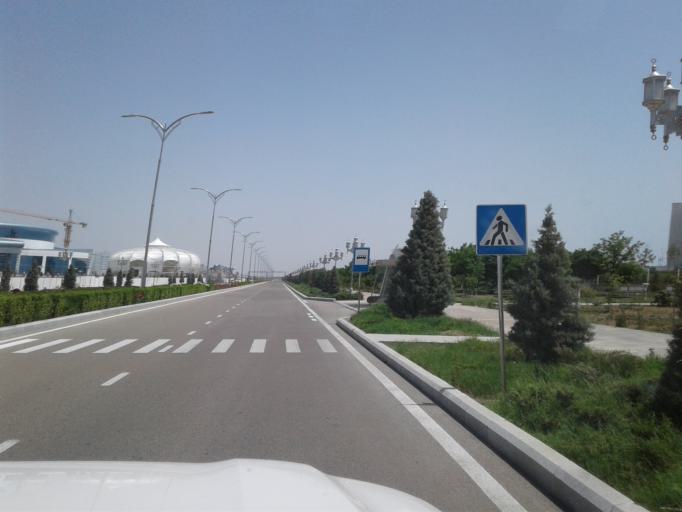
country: TM
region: Balkan
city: Turkmenbasy
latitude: 39.9614
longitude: 52.8392
